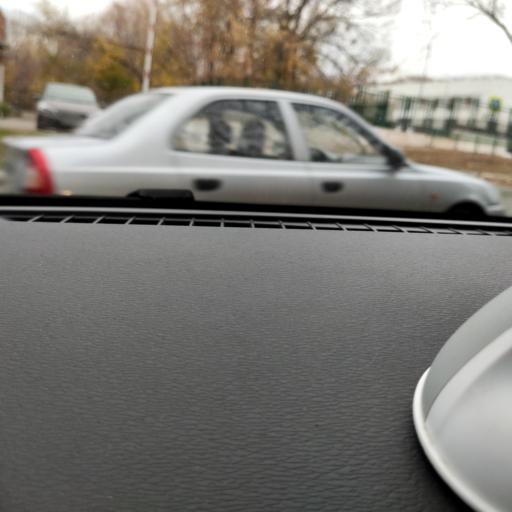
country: RU
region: Samara
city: Samara
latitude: 53.2596
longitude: 50.2025
